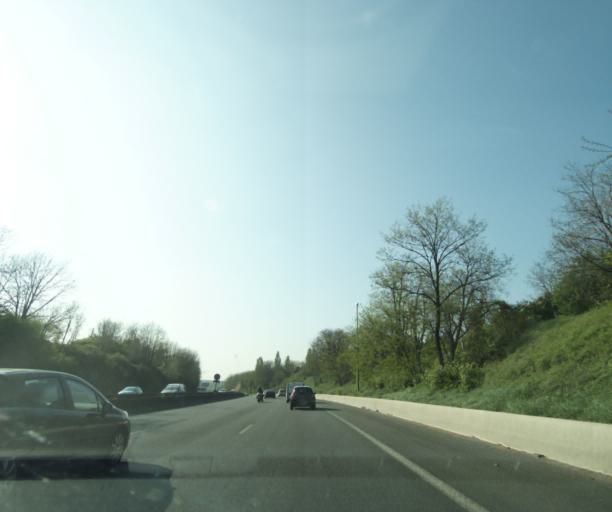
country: FR
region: Ile-de-France
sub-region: Departement de l'Essonne
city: Morsang-sur-Orge
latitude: 48.6665
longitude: 2.3614
